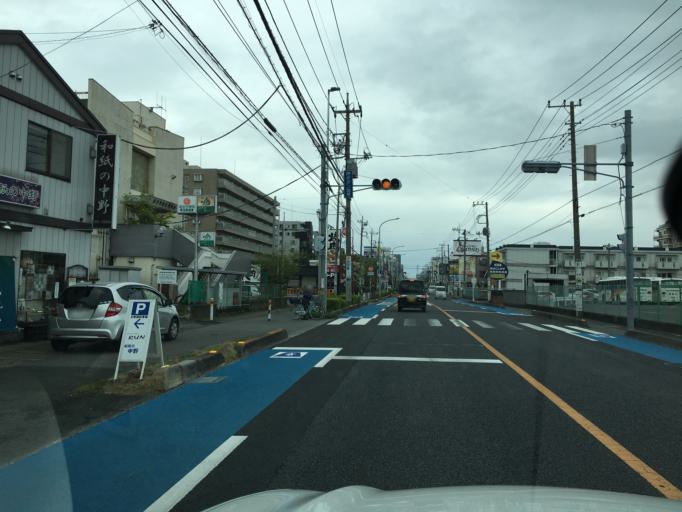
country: JP
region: Saitama
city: Koshigaya
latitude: 35.8686
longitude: 139.7946
